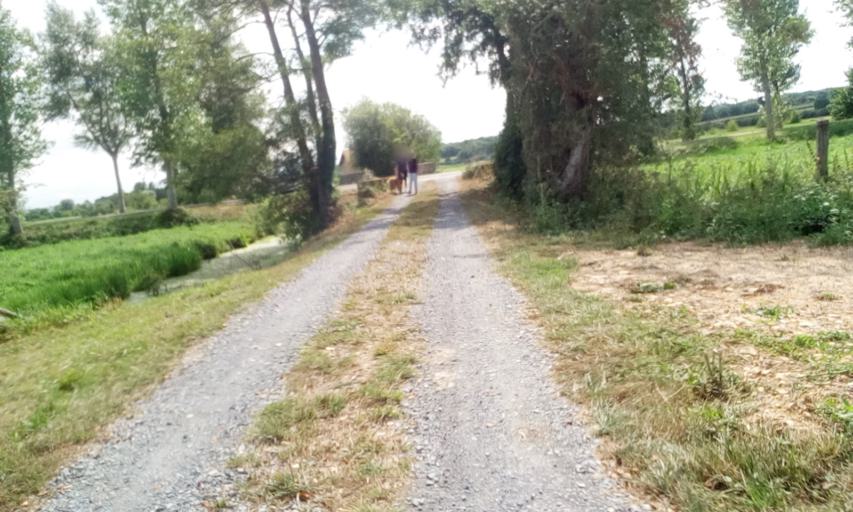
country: FR
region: Lower Normandy
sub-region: Departement du Calvados
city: Bavent
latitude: 49.2279
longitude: -0.1716
